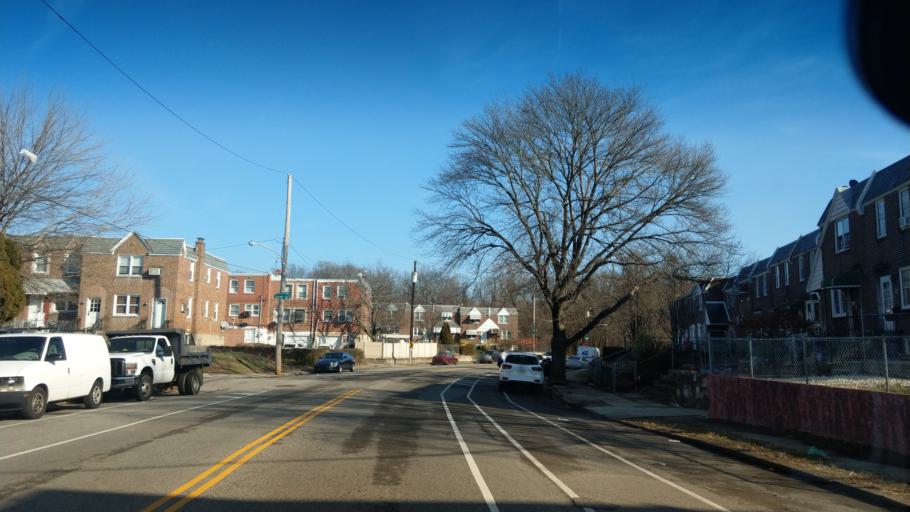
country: US
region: Pennsylvania
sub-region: Montgomery County
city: Rockledge
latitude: 40.0291
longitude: -75.1148
